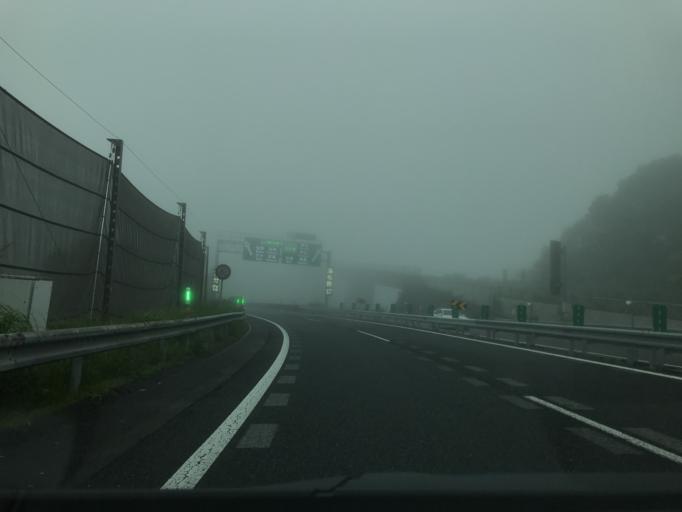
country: JP
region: Oita
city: Hiji
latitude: 33.3552
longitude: 131.4463
